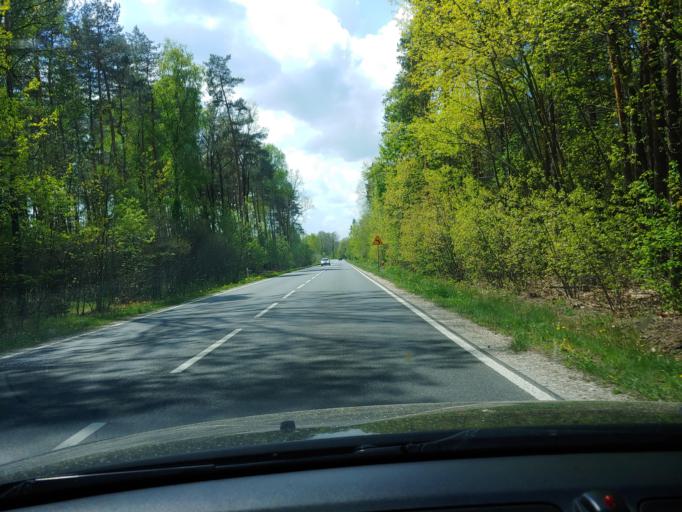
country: PL
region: Lesser Poland Voivodeship
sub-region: Powiat tarnowski
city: Jodlowka-Walki
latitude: 50.1159
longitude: 21.1184
